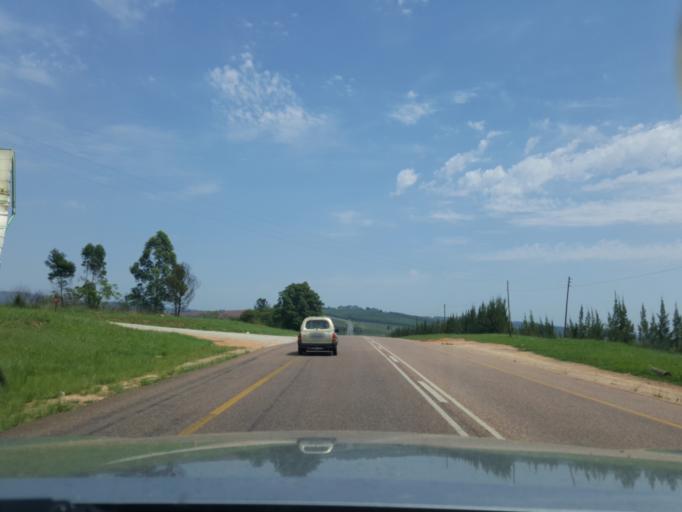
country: ZA
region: Mpumalanga
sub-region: Ehlanzeni District
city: White River
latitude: -25.3010
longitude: 31.0294
